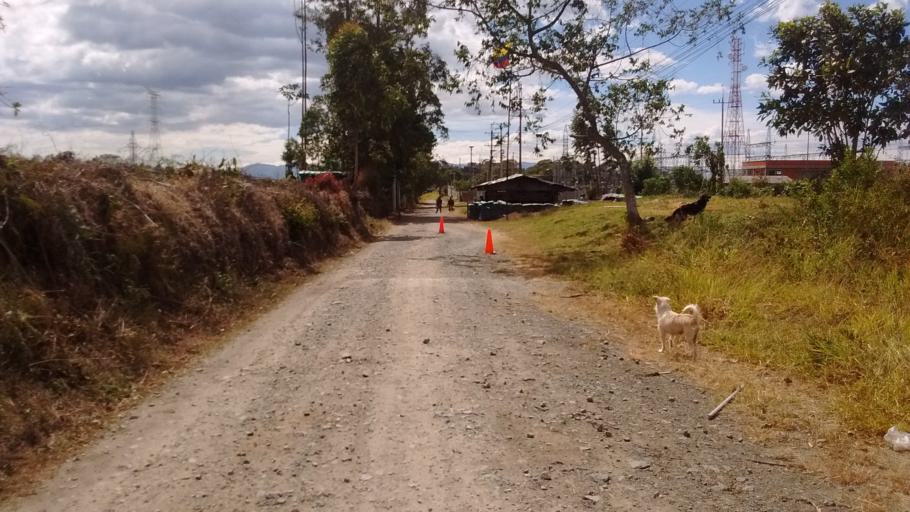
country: CO
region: Cauca
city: Popayan
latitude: 2.4974
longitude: -76.5930
